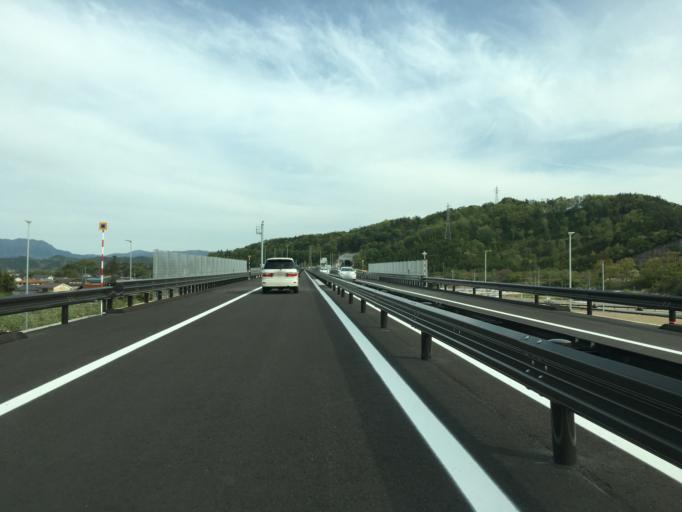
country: JP
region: Fukushima
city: Hobaramachi
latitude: 37.8130
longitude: 140.5349
